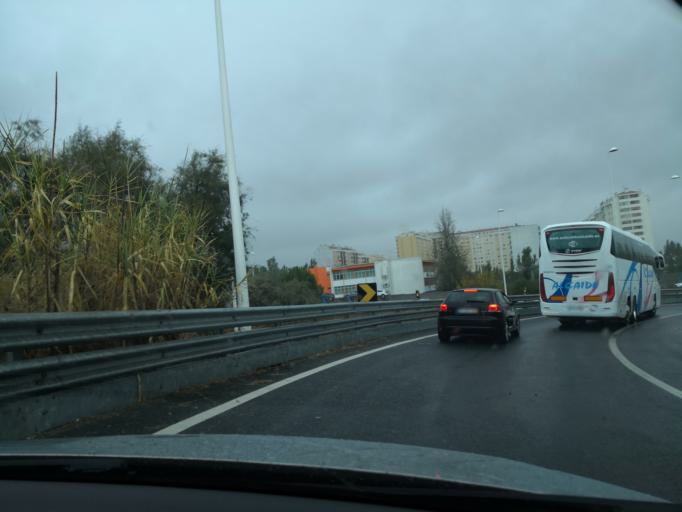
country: PT
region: Lisbon
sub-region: Loures
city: Sacavem
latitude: 38.7865
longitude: -9.1052
